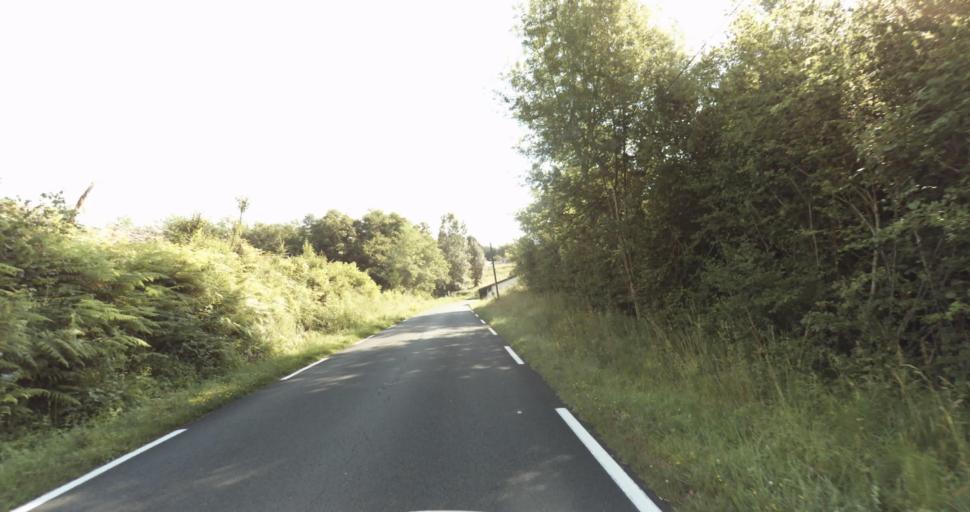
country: FR
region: Aquitaine
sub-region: Departement de la Gironde
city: Bazas
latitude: 44.4263
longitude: -0.2429
